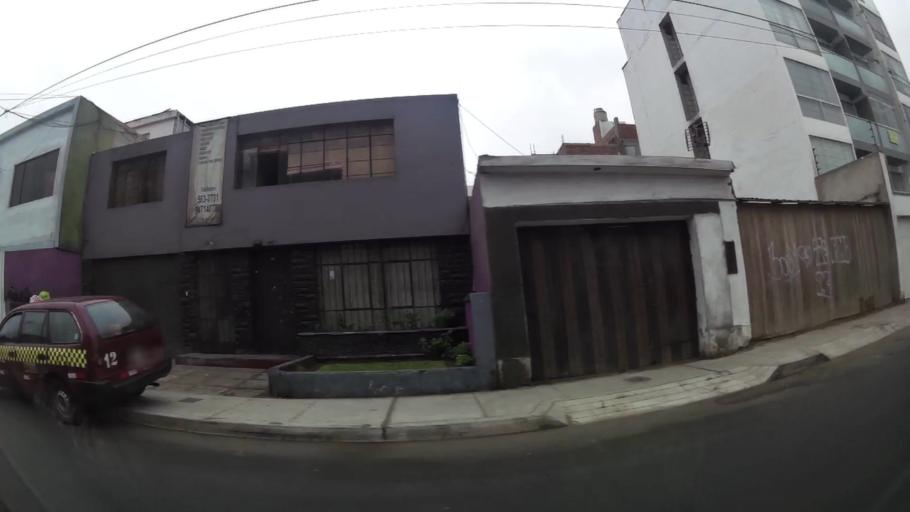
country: PE
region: Lima
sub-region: Lima
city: San Isidro
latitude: -12.0901
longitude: -77.0854
